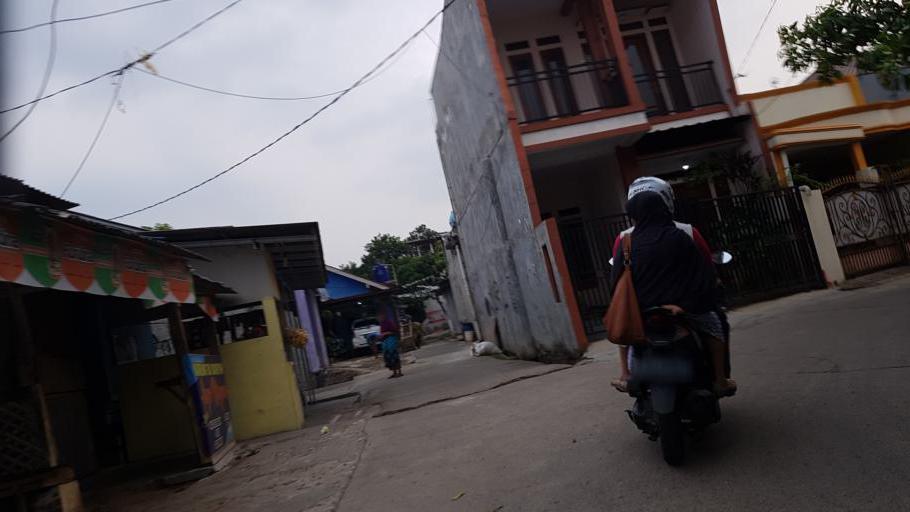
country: ID
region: West Java
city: Depok
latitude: -6.3738
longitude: 106.7954
